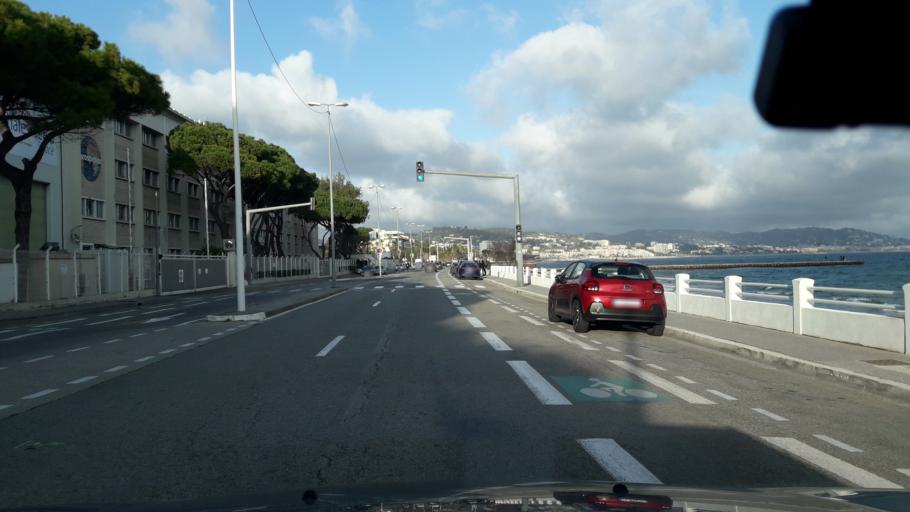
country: FR
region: Provence-Alpes-Cote d'Azur
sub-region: Departement des Alpes-Maritimes
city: Mandelieu-la-Napoule
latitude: 43.5376
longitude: 6.9548
